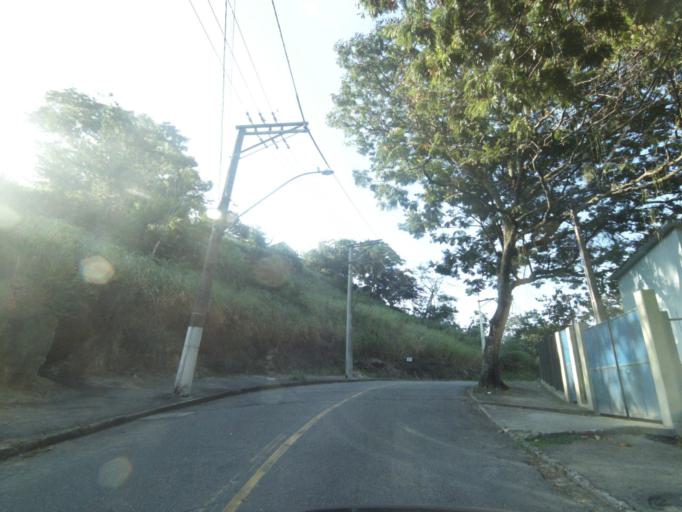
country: BR
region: Rio de Janeiro
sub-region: Niteroi
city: Niteroi
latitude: -22.8886
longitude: -43.0937
